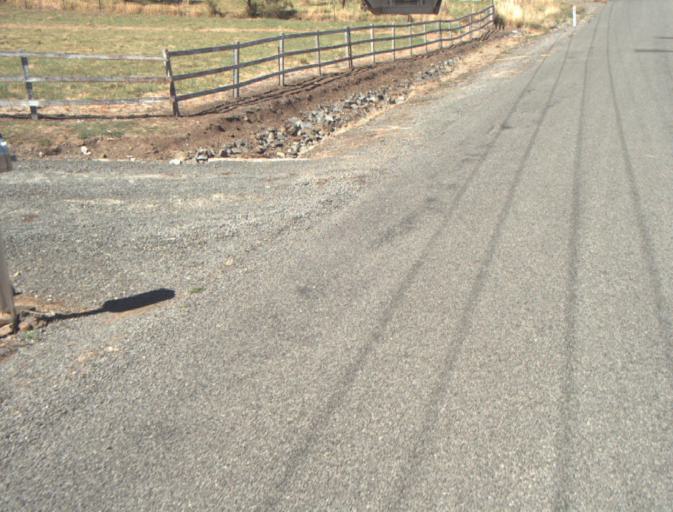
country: AU
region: Tasmania
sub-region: Launceston
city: Newstead
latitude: -41.3539
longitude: 147.3036
